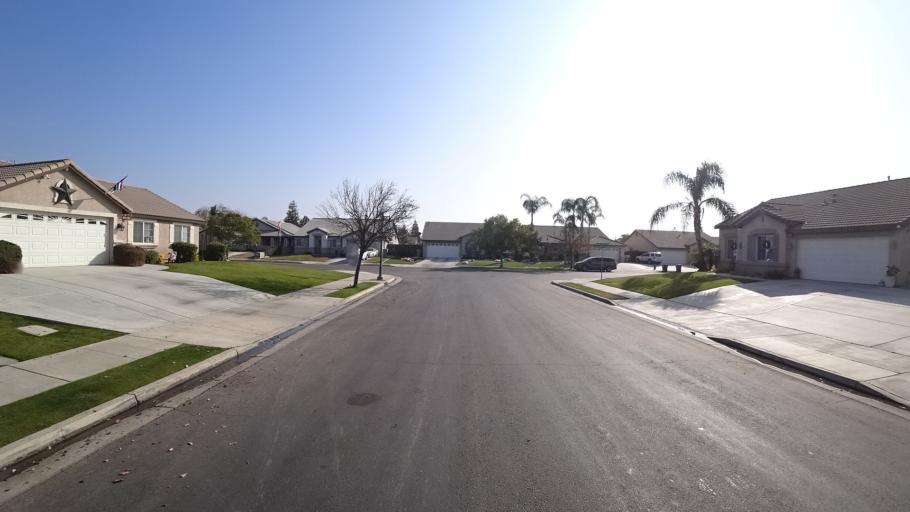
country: US
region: California
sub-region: Kern County
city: Greenacres
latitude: 35.4145
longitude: -119.1183
